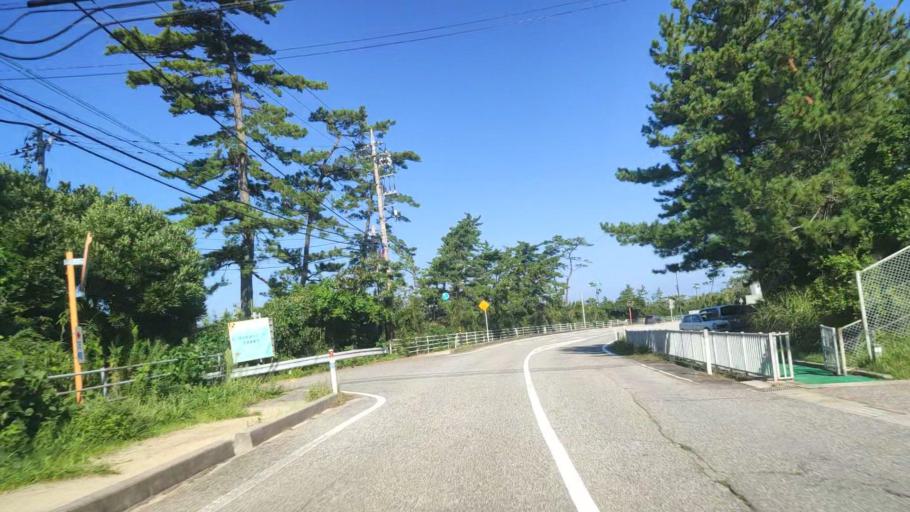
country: JP
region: Ishikawa
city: Hakui
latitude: 37.0552
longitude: 136.7248
